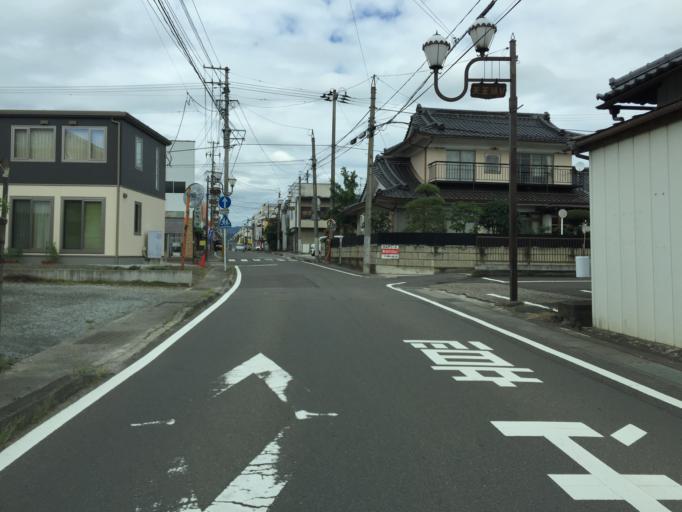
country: JP
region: Fukushima
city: Hobaramachi
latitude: 37.8179
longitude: 140.5015
